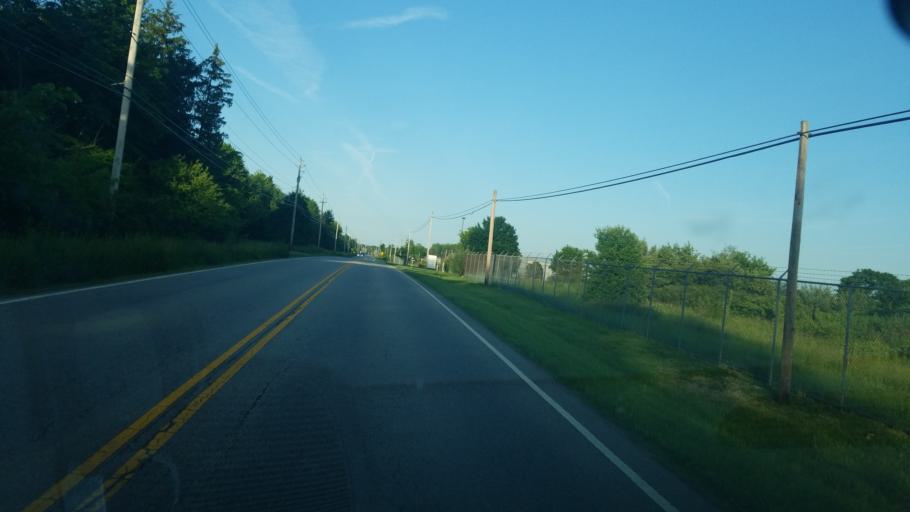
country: US
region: Ohio
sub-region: Trumbull County
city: Lordstown
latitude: 41.0994
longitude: -80.8946
